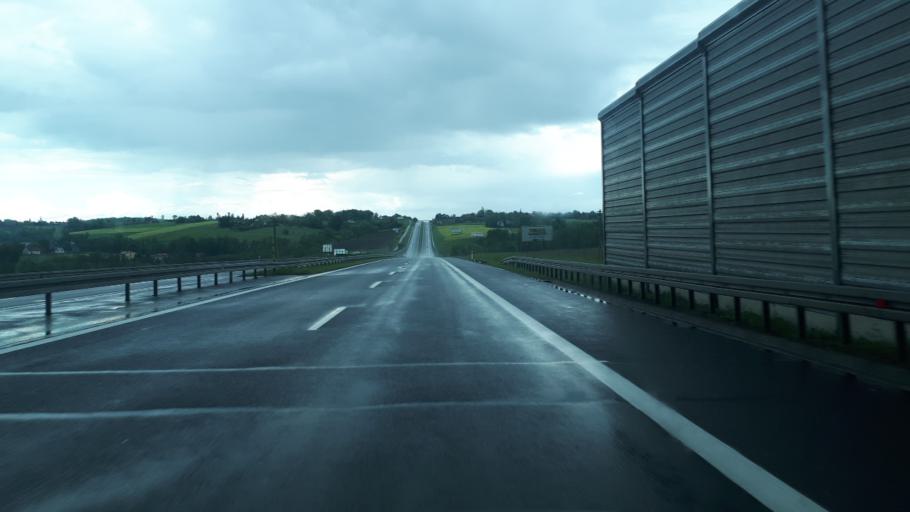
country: PL
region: Silesian Voivodeship
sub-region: Powiat cieszynski
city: Debowiec
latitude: 49.7807
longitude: 18.7391
